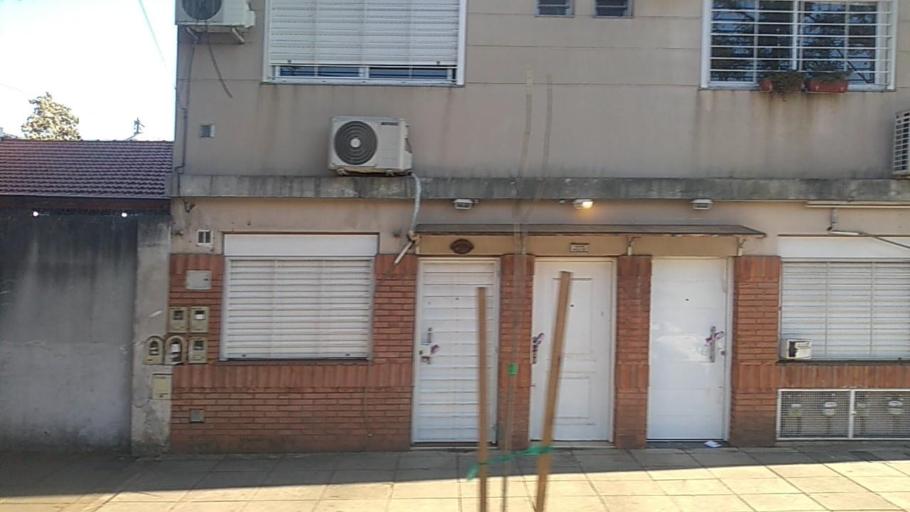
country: AR
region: Buenos Aires F.D.
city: Villa Santa Rita
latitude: -34.6236
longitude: -58.4971
